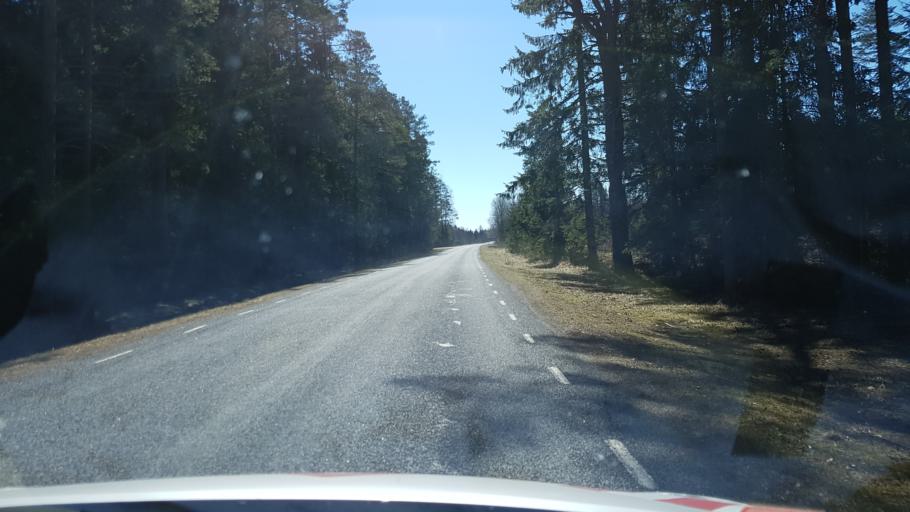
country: EE
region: Laeaene-Virumaa
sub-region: Haljala vald
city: Haljala
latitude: 59.4958
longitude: 26.2429
